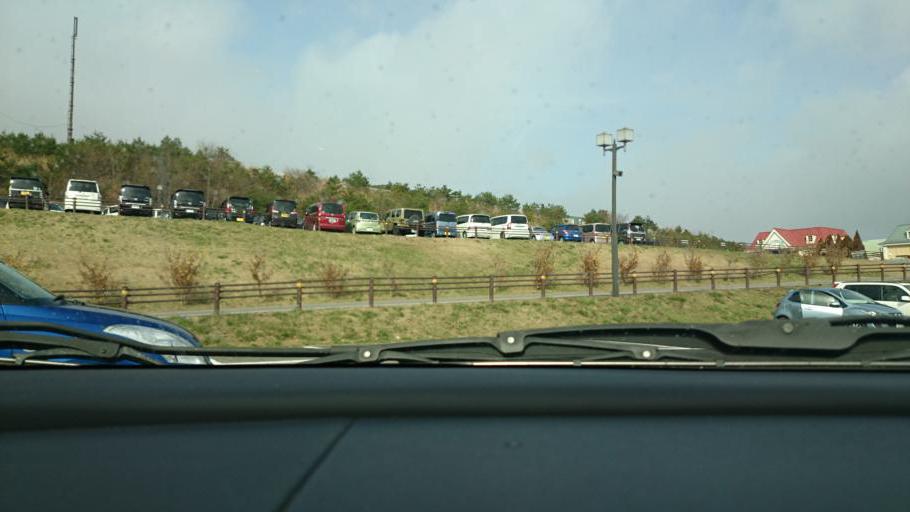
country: JP
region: Tochigi
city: Kuroiso
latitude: 37.1281
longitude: 140.0370
